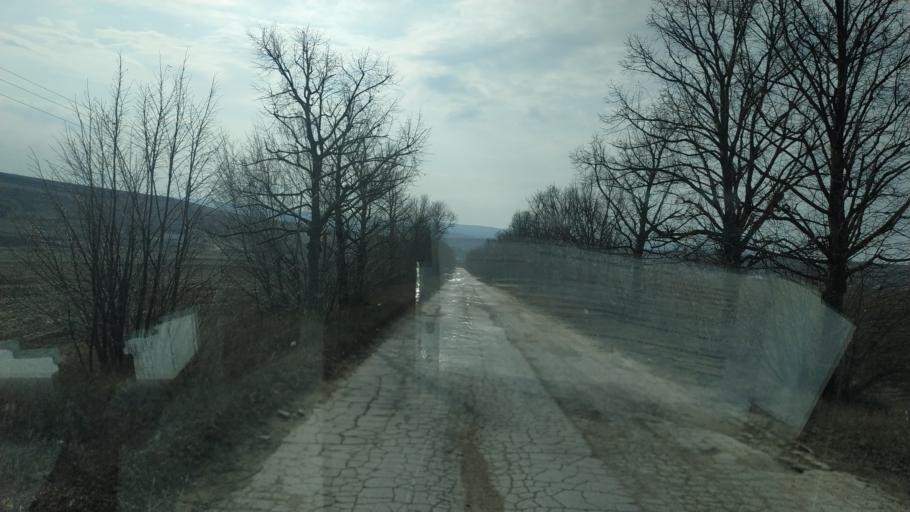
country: MD
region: Anenii Noi
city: Anenii Noi
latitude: 46.9379
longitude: 29.1085
